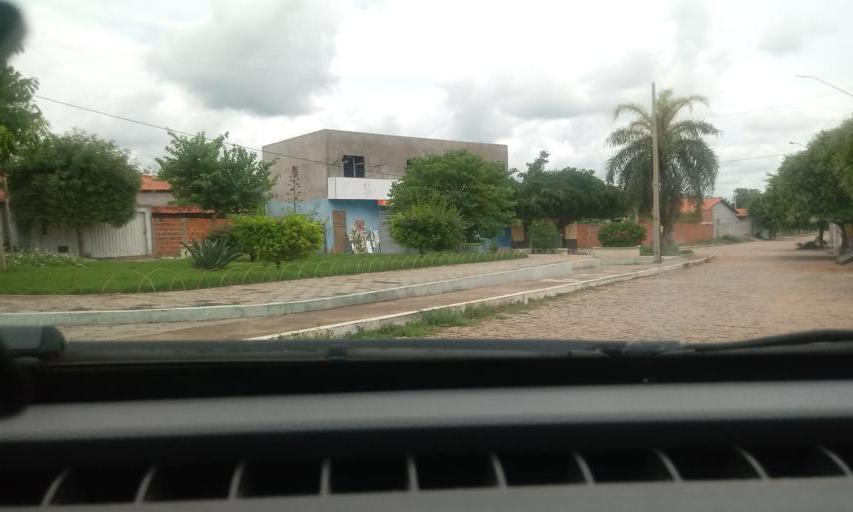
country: BR
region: Bahia
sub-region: Riacho De Santana
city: Riacho de Santana
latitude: -13.9121
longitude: -42.8464
